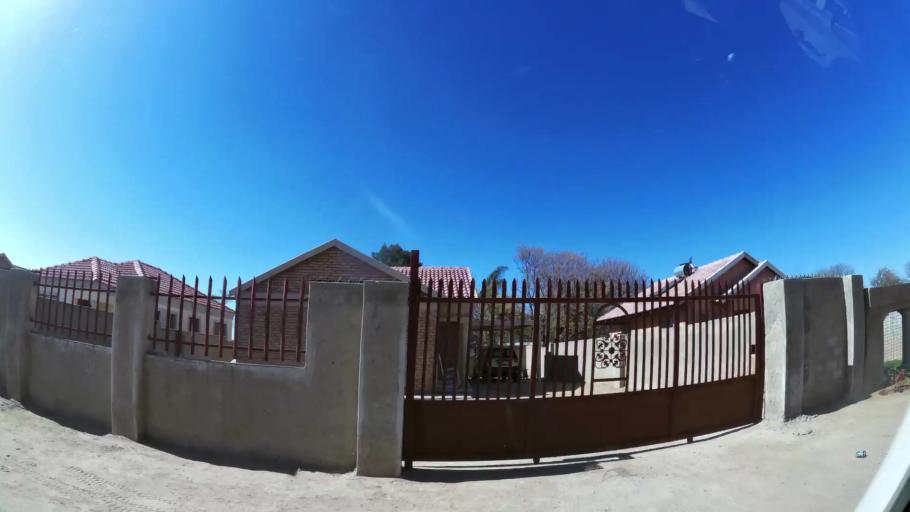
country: ZA
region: Limpopo
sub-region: Capricorn District Municipality
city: Polokwane
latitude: -23.8588
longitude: 29.4262
